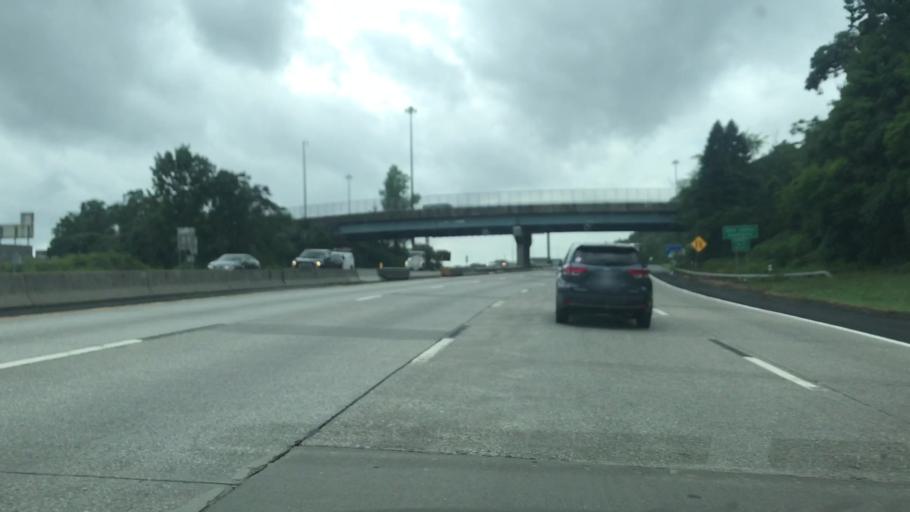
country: US
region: New York
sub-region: Rockland County
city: Suffern
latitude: 41.1138
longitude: -74.1621
